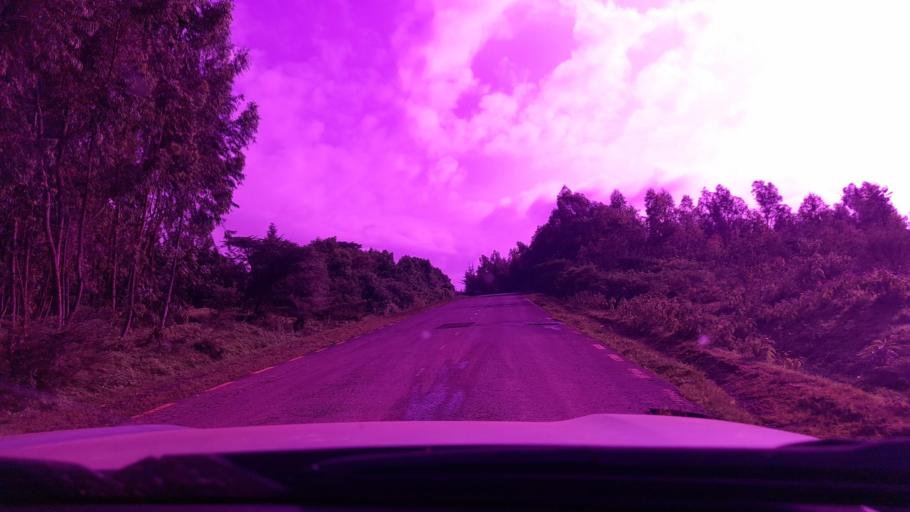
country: ET
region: Oromiya
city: Bedele
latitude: 8.2099
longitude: 36.4444
